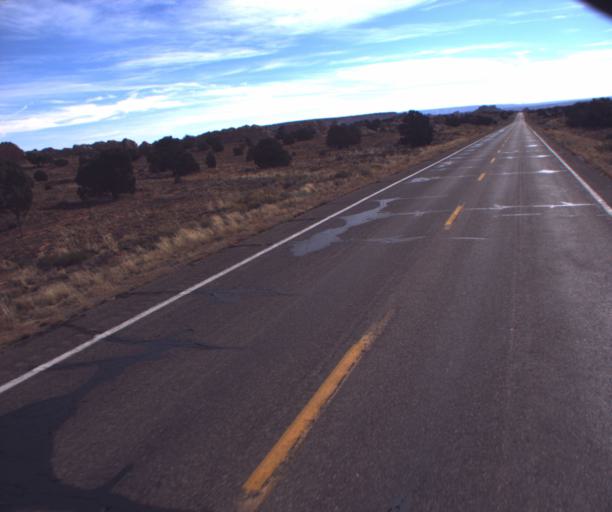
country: US
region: Arizona
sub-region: Coconino County
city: Kaibito
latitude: 36.6498
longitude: -111.2338
